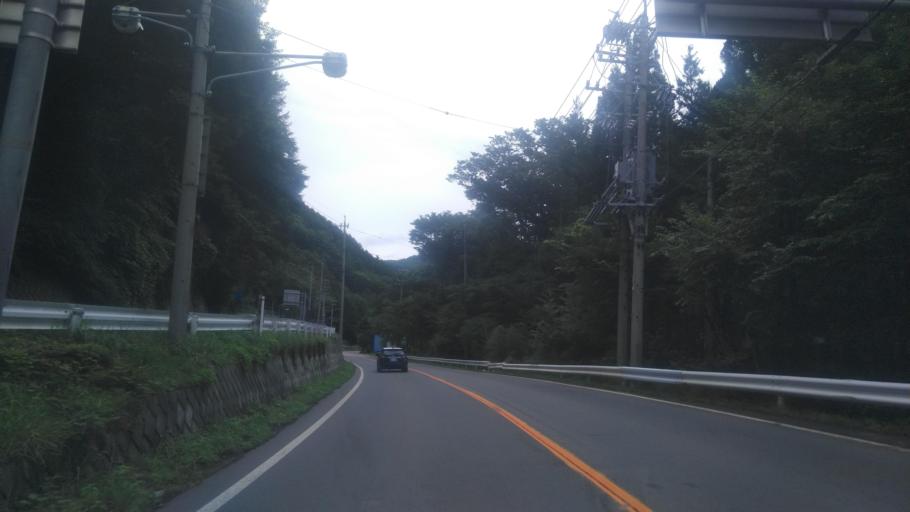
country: JP
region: Nagano
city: Ueda
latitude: 36.4894
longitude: 138.3599
